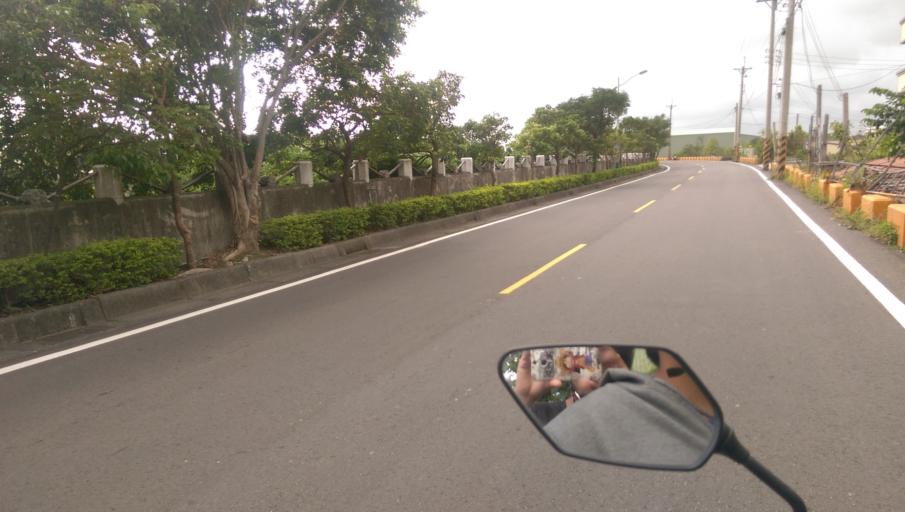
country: TW
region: Taiwan
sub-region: Hsinchu
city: Hsinchu
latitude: 24.8051
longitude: 120.9320
